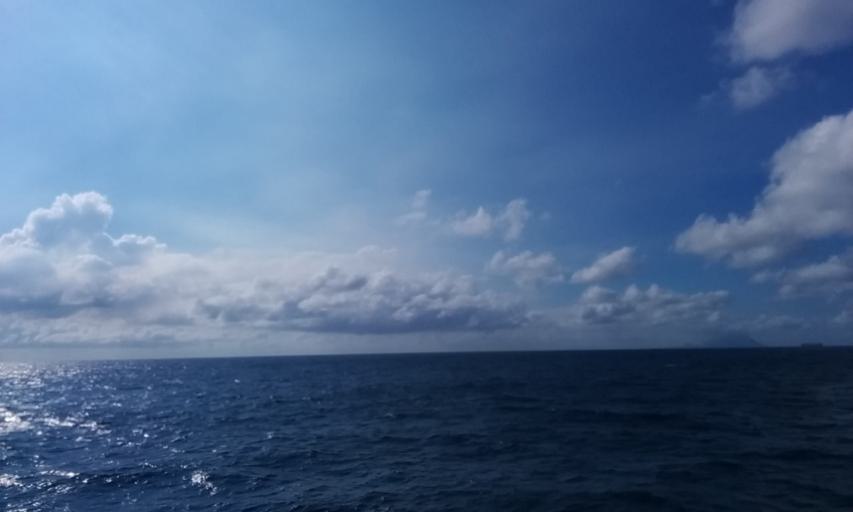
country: JP
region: Kagoshima
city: Nishinoomote
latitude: 30.6692
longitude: 130.6014
